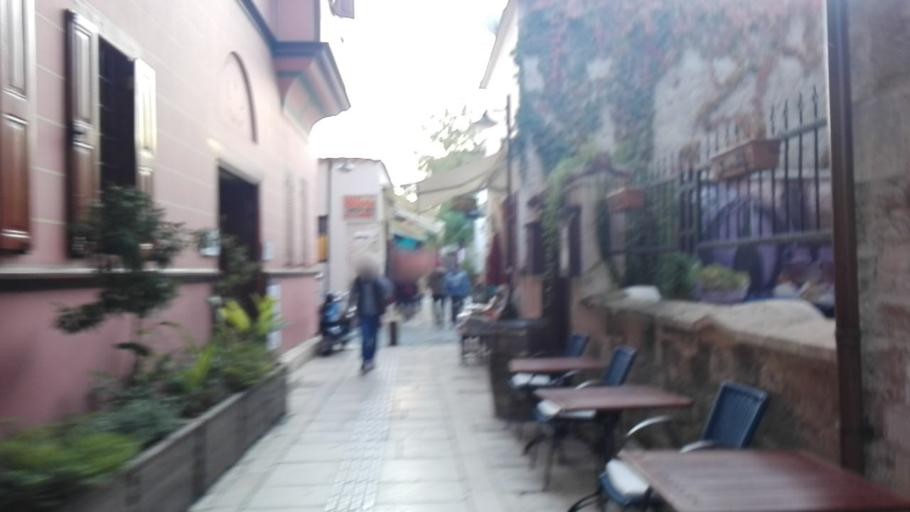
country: TR
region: Antalya
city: Antalya
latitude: 36.8846
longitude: 30.7077
